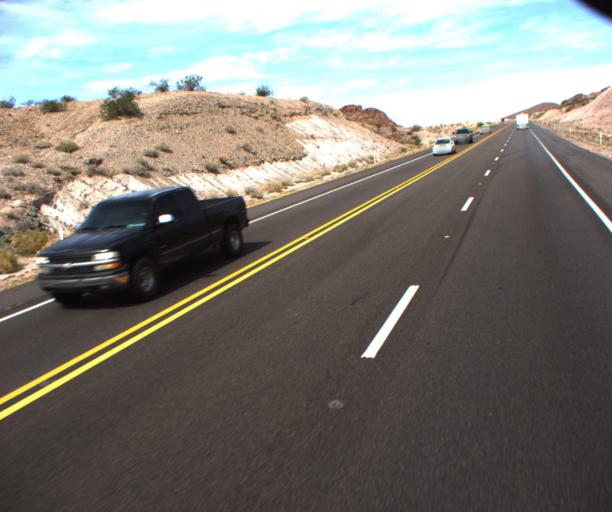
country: US
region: Arizona
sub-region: Mohave County
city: Desert Hills
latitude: 34.6229
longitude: -114.3368
